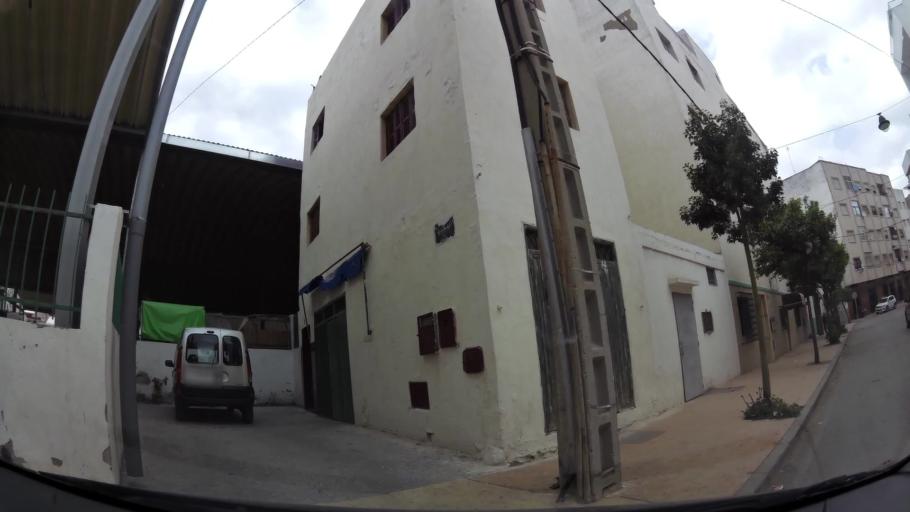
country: MA
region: Tanger-Tetouan
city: Tetouan
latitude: 35.5696
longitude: -5.3533
